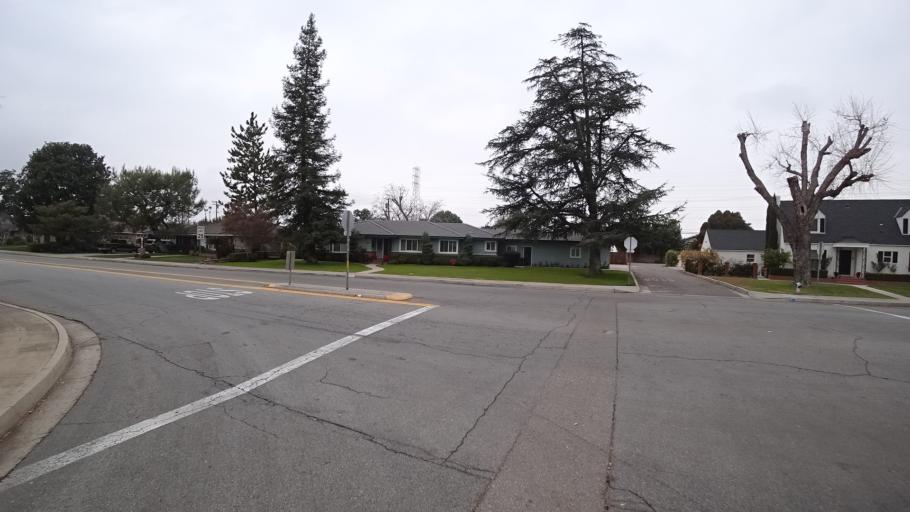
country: US
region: California
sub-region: Kern County
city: Bakersfield
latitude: 35.3867
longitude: -119.0314
